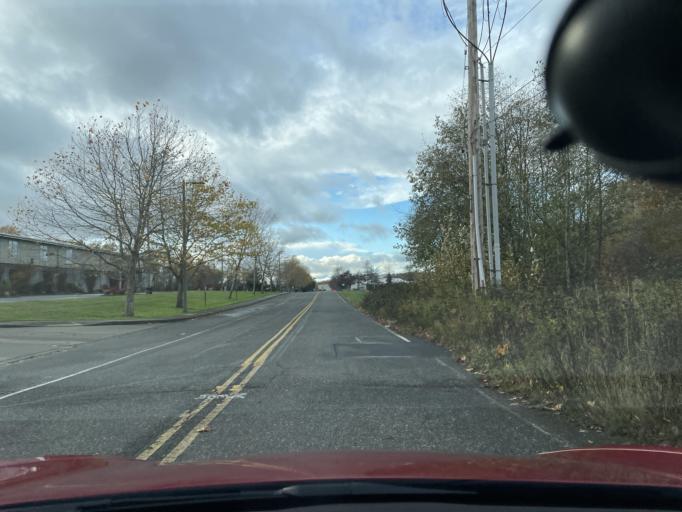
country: US
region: Washington
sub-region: Whatcom County
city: Marietta-Alderwood
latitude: 48.7896
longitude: -122.5269
